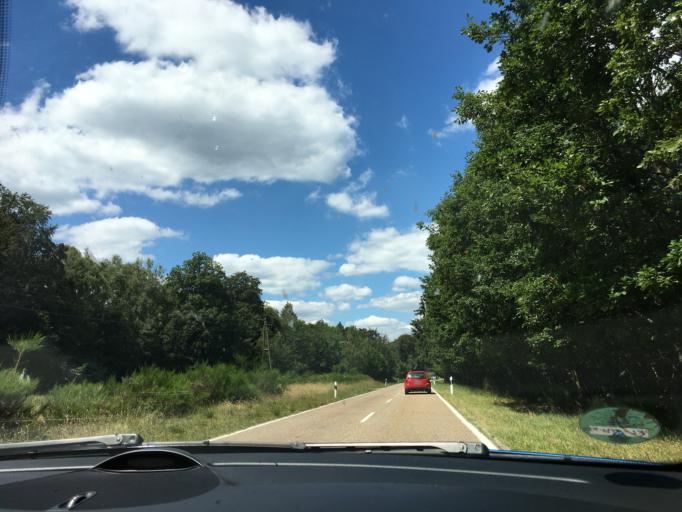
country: DE
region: Rheinland-Pfalz
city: Hauenstein
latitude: 49.2342
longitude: 7.8370
